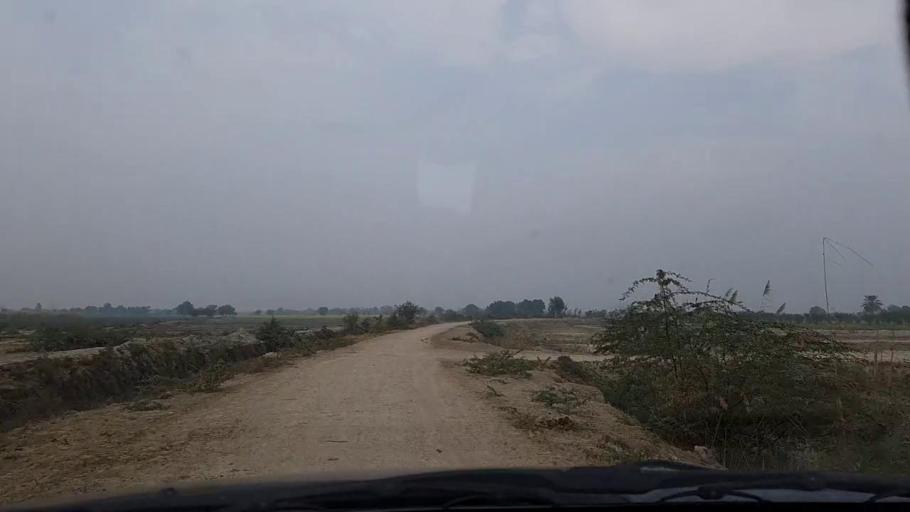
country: PK
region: Sindh
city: Tando Mittha Khan
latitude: 25.8062
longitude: 69.3753
